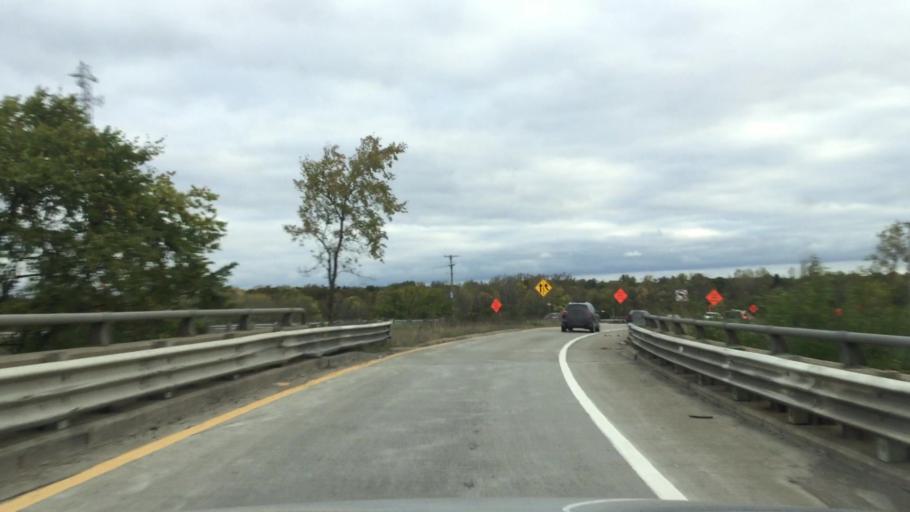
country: US
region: Michigan
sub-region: Genesee County
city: Flint
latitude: 42.9832
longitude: -83.7294
